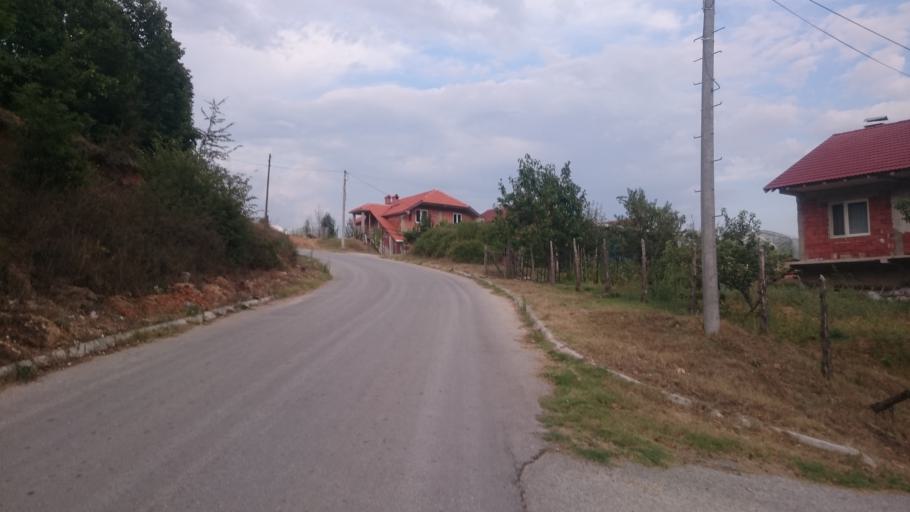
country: MK
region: Makedonski Brod
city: Makedonski Brod
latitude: 41.5203
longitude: 21.2145
